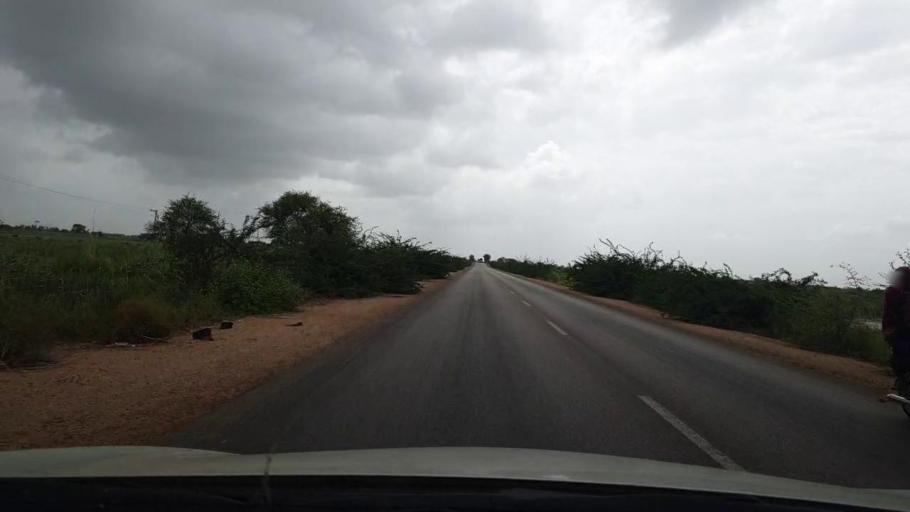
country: PK
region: Sindh
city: Mirpur Batoro
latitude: 24.6001
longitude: 68.2280
